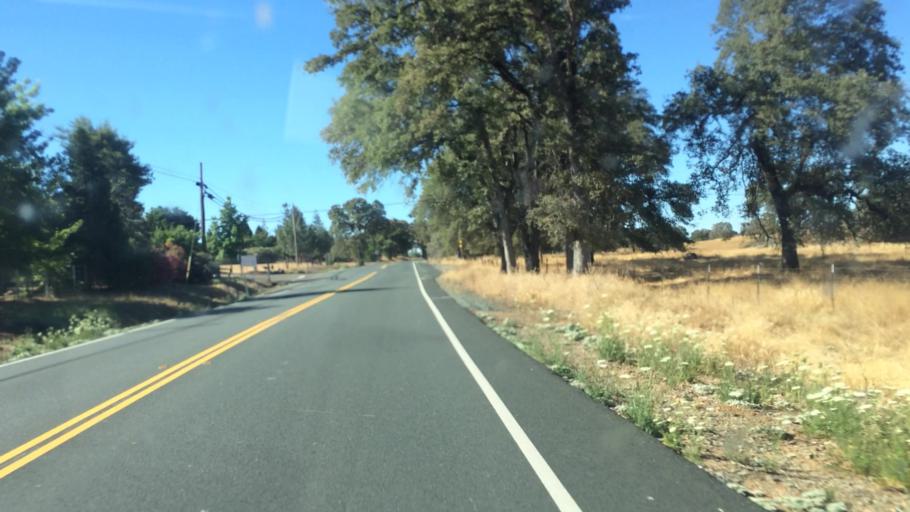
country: US
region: California
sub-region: El Dorado County
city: Deer Park
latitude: 38.6405
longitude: -120.8509
